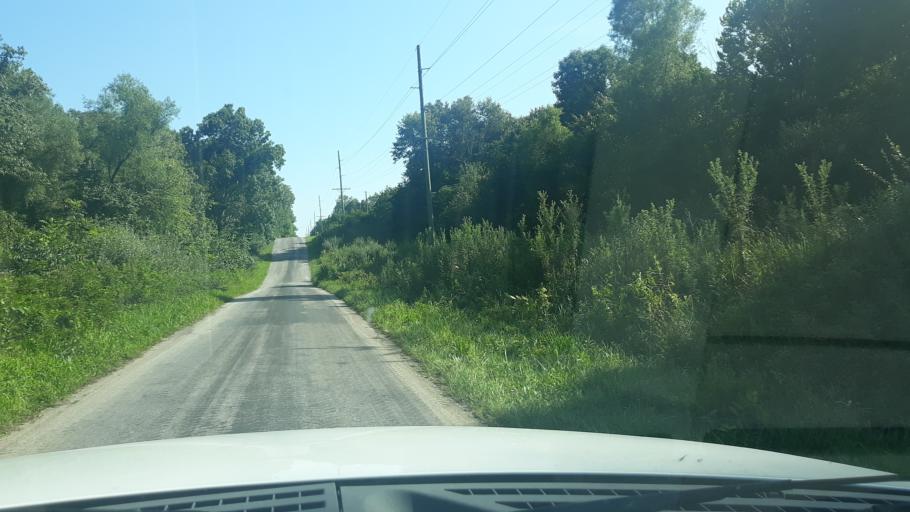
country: US
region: Illinois
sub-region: Saline County
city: Harrisburg
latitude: 37.8574
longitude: -88.5963
